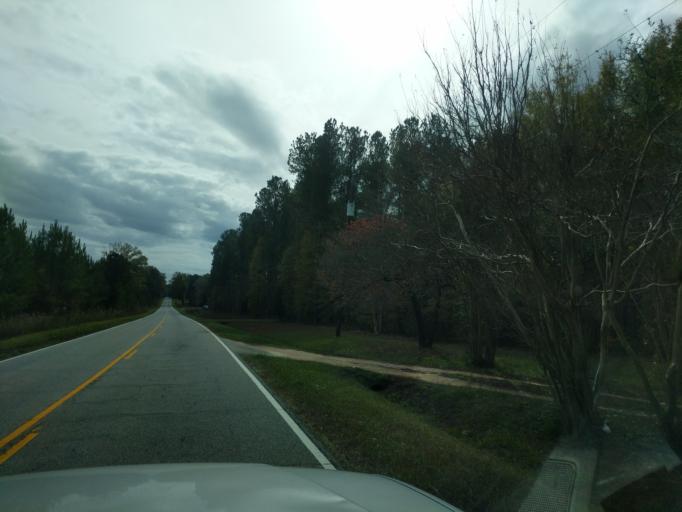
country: US
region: South Carolina
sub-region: Saluda County
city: Saluda
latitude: 34.0936
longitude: -81.8288
